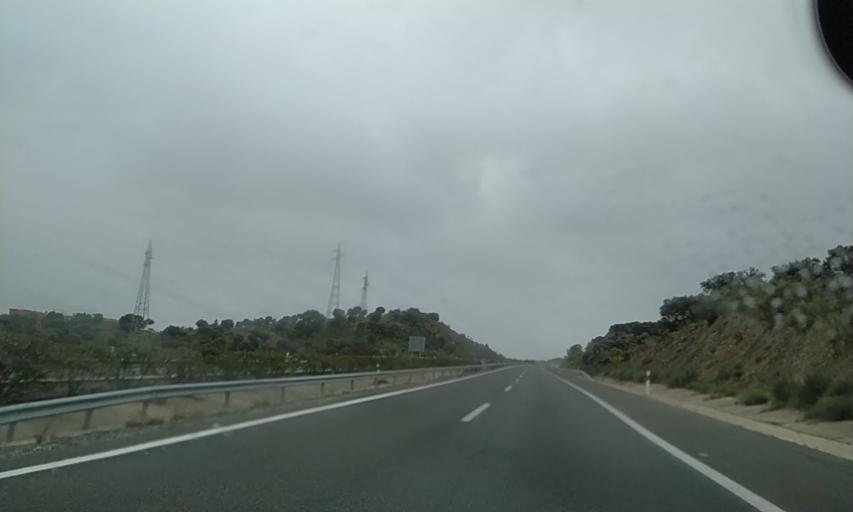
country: ES
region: Extremadura
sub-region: Provincia de Caceres
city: Plasencia
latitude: 40.0193
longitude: -6.1283
